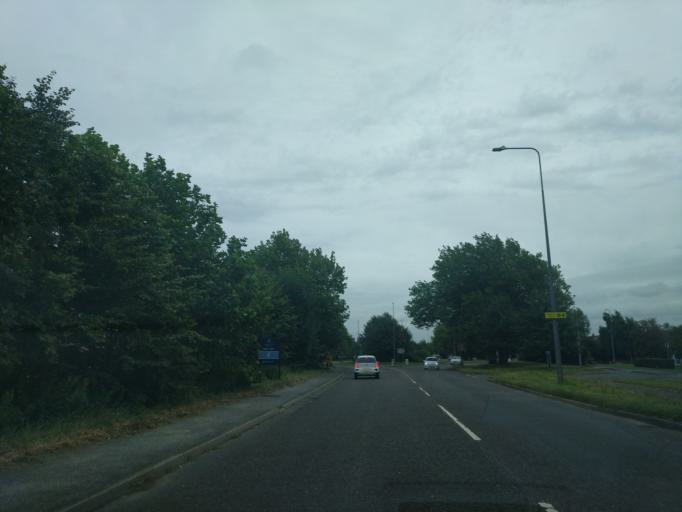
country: GB
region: England
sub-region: Lincolnshire
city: Great Gonerby
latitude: 52.9173
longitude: -0.6651
